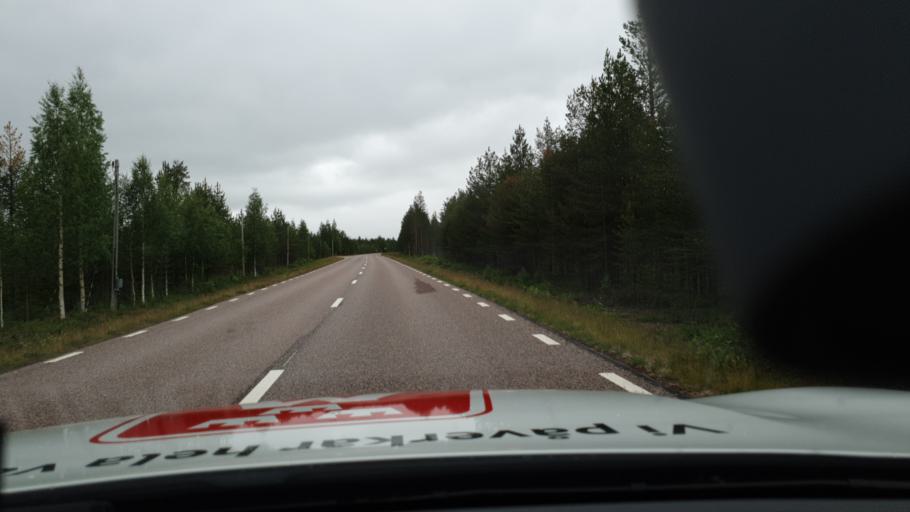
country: FI
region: Lapland
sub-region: Tunturi-Lappi
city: Kolari
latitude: 67.0377
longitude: 23.7028
